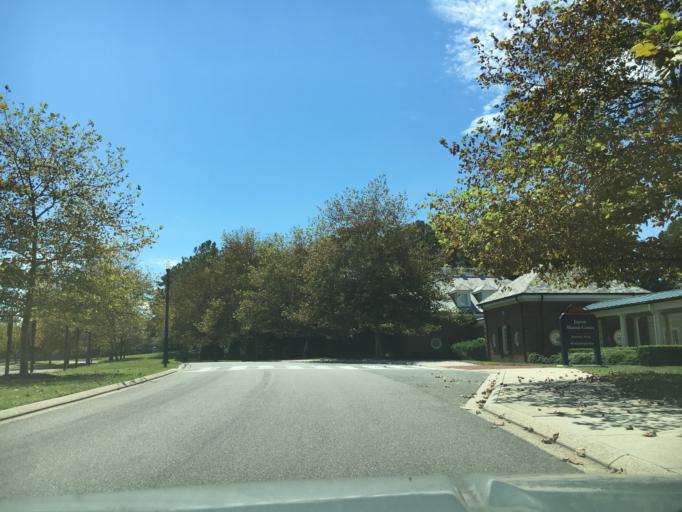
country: US
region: Virginia
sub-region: Henrico County
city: Tuckahoe
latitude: 37.5746
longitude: -77.5456
